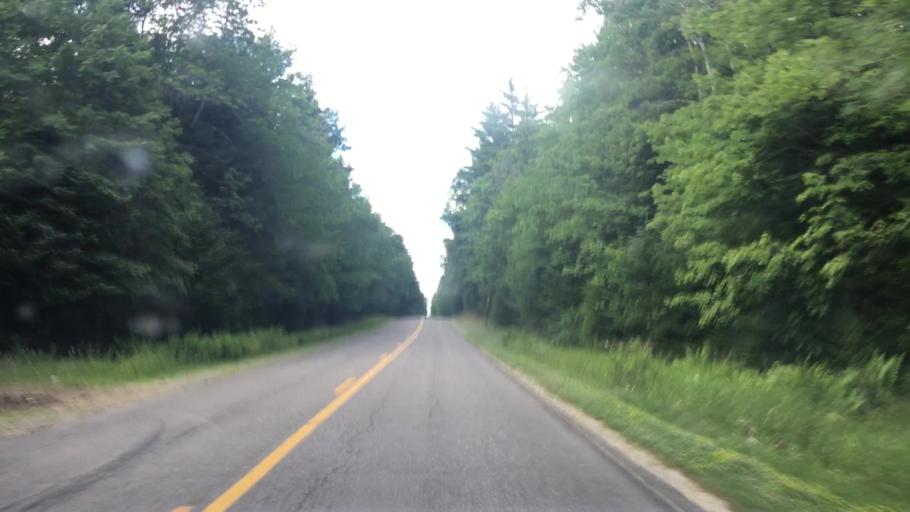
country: US
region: Maine
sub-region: Franklin County
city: Chesterville
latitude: 44.5948
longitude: -70.0856
